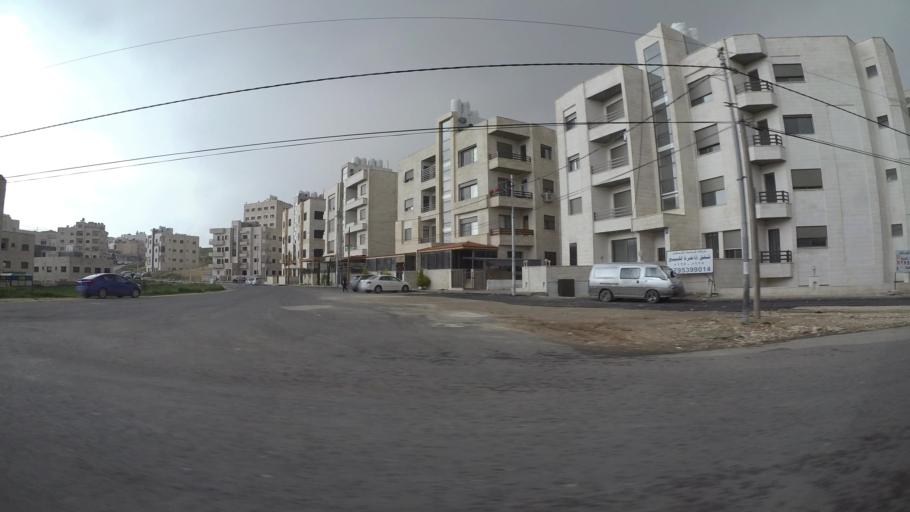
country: JO
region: Amman
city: Umm as Summaq
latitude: 31.8825
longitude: 35.8533
